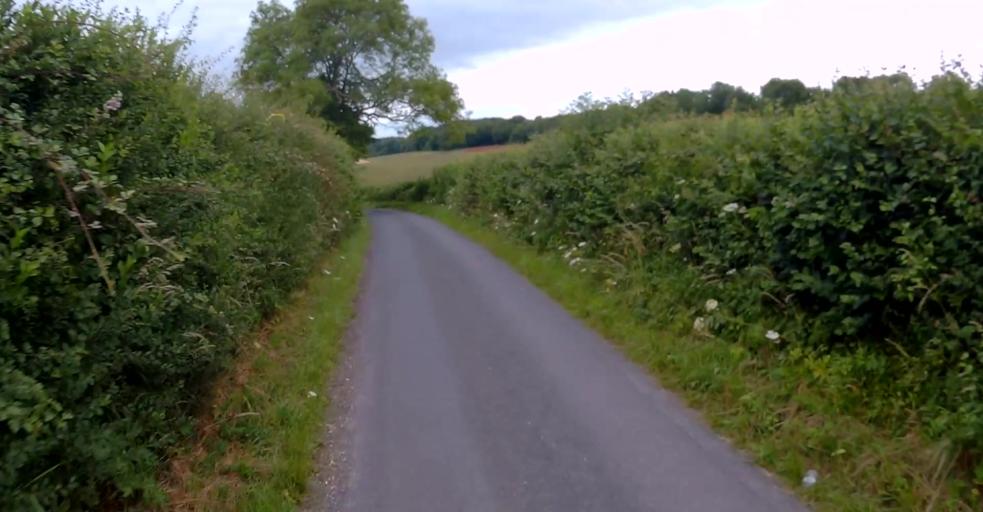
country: GB
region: England
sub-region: Hampshire
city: Kings Worthy
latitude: 51.0605
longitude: -1.2070
